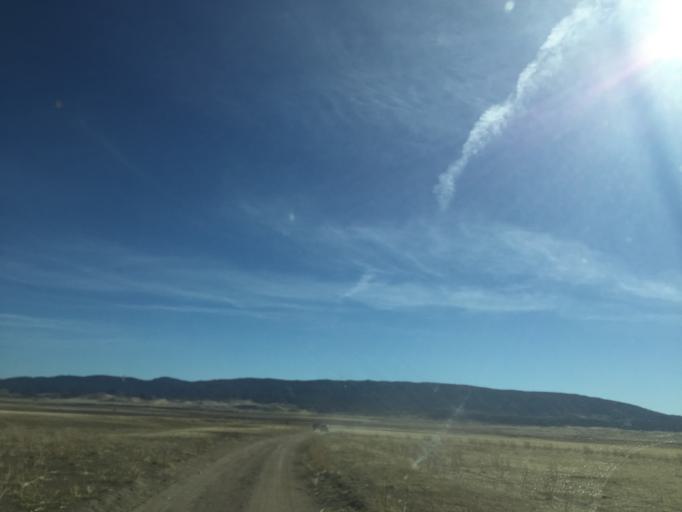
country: US
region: California
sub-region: Kern County
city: Lebec
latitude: 34.8432
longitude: -118.6664
